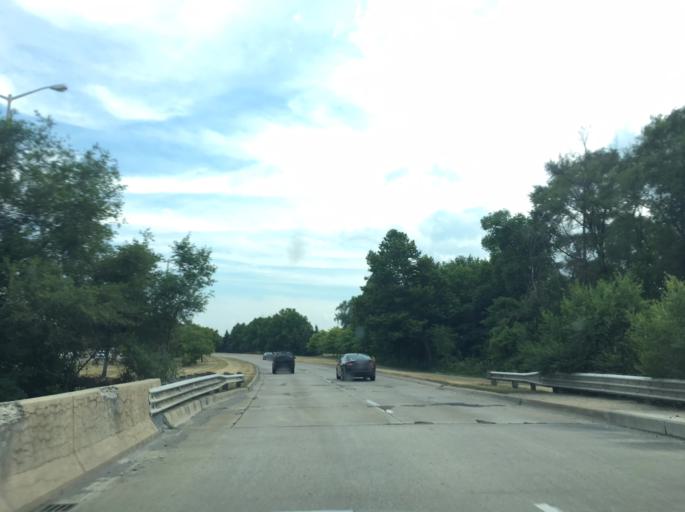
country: US
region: Michigan
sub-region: Macomb County
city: Sterling Heights
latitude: 42.5725
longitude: -82.9901
